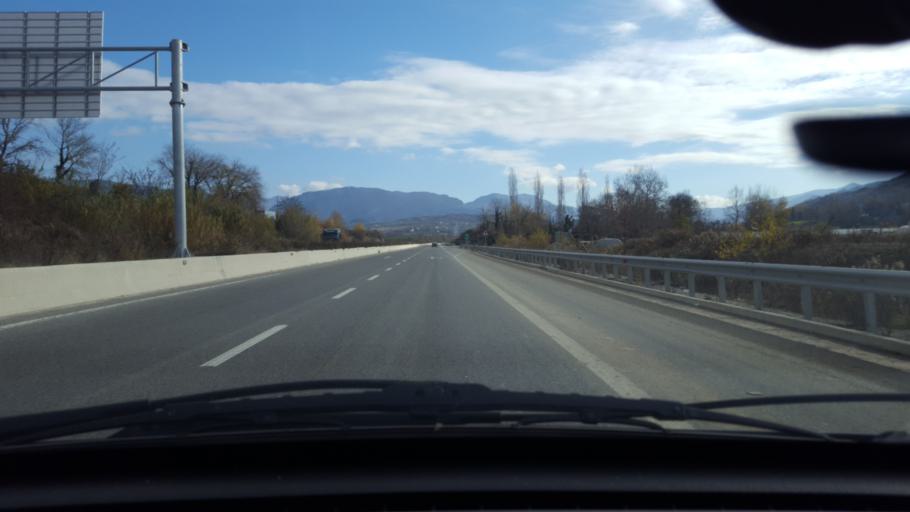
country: AL
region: Tirane
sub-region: Rrethi i Tiranes
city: Petrele
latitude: 41.2627
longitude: 19.8777
